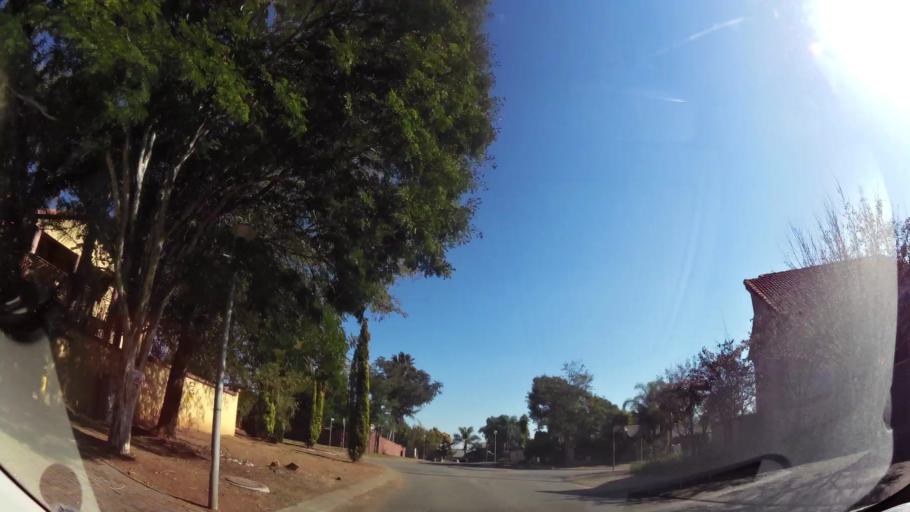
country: ZA
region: Gauteng
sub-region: City of Tshwane Metropolitan Municipality
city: Centurion
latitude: -25.8624
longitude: 28.1788
